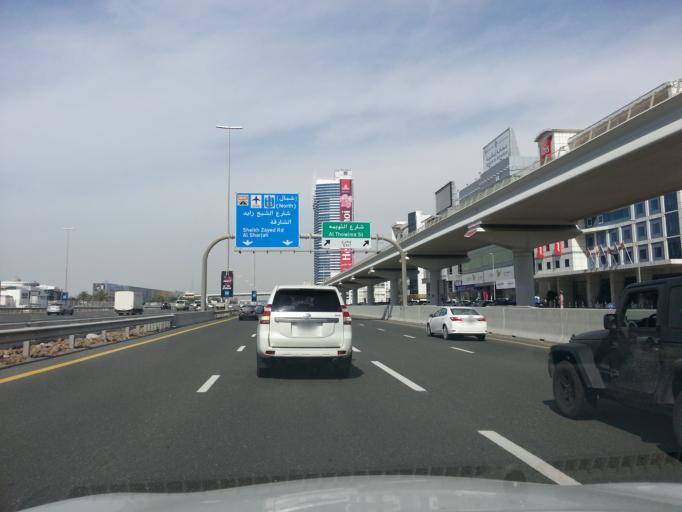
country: AE
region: Dubai
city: Dubai
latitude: 25.1088
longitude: 55.1821
